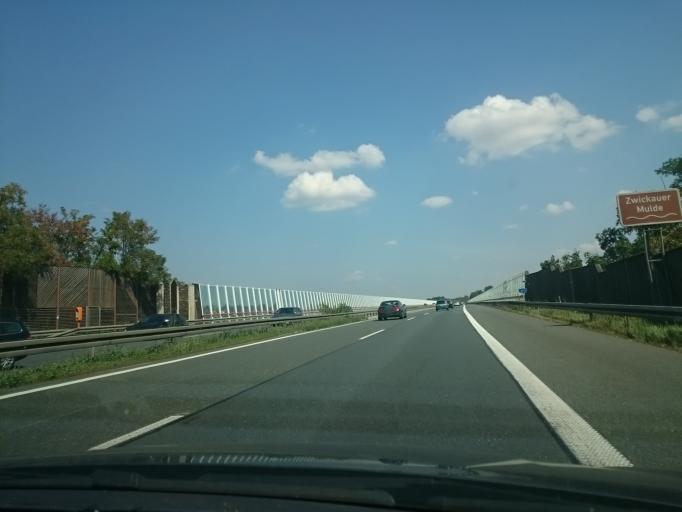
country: DE
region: Saxony
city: Wilkau-Hasslau
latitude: 50.6687
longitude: 12.5238
